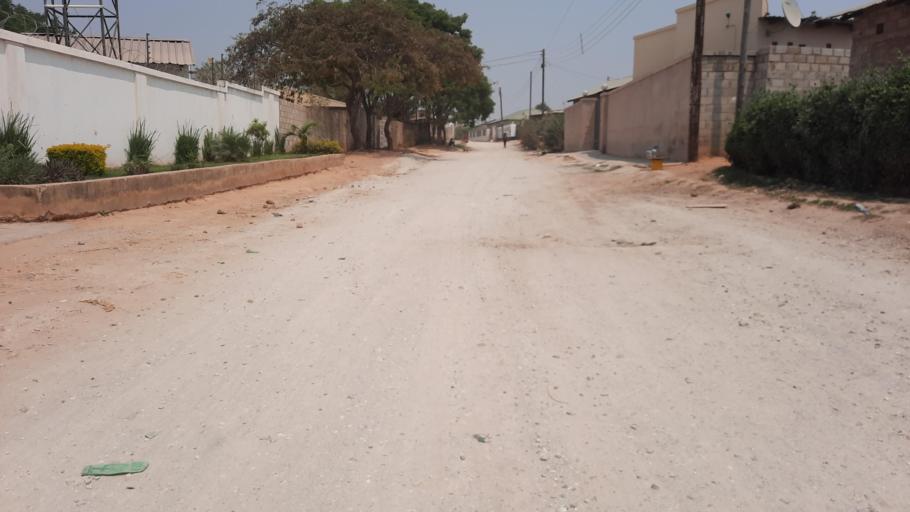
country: ZM
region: Lusaka
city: Lusaka
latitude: -15.4088
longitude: 28.3731
